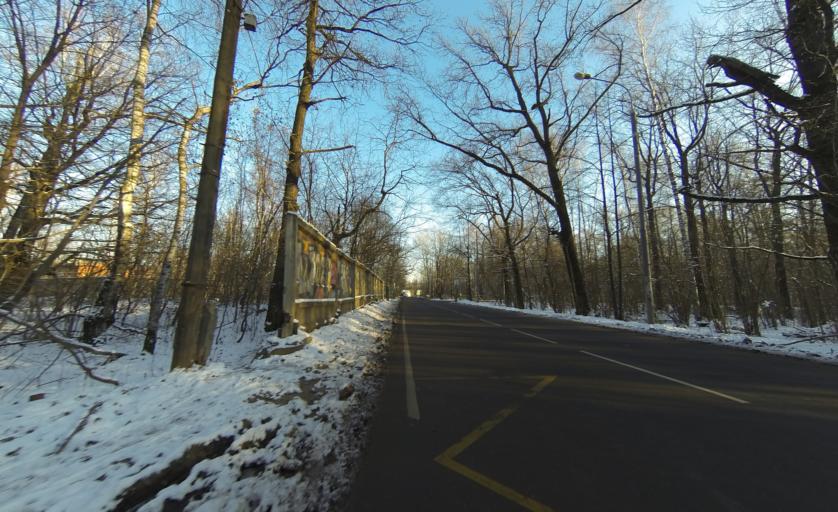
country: RU
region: Moscow
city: Rostokino
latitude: 55.8308
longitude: 37.6931
